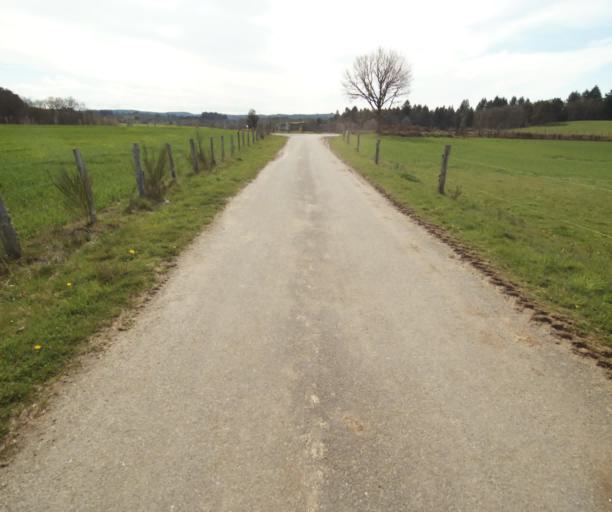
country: FR
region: Limousin
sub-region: Departement de la Correze
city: Correze
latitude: 45.3570
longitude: 1.9107
